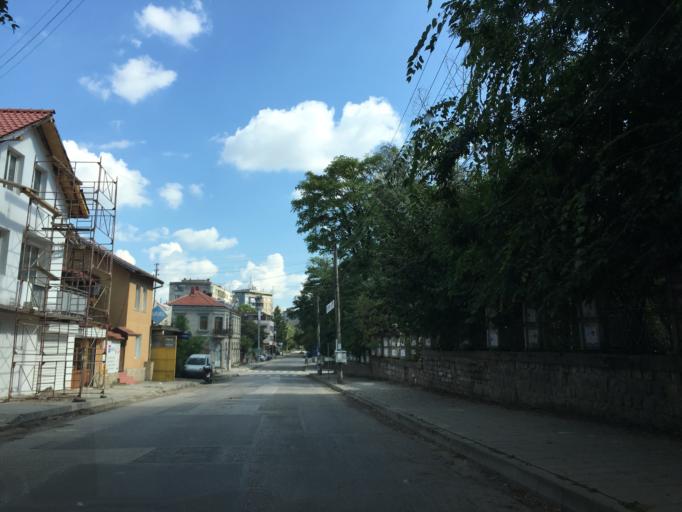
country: BG
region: Montana
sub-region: Obshtina Lom
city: Lom
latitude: 43.8310
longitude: 23.2327
